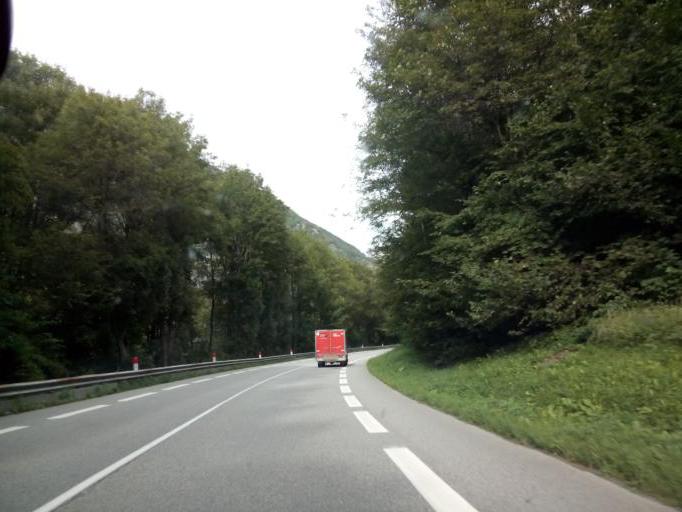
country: FR
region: Rhone-Alpes
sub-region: Departement de l'Isere
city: Livet-et-Gavet
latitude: 45.1178
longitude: 5.9711
